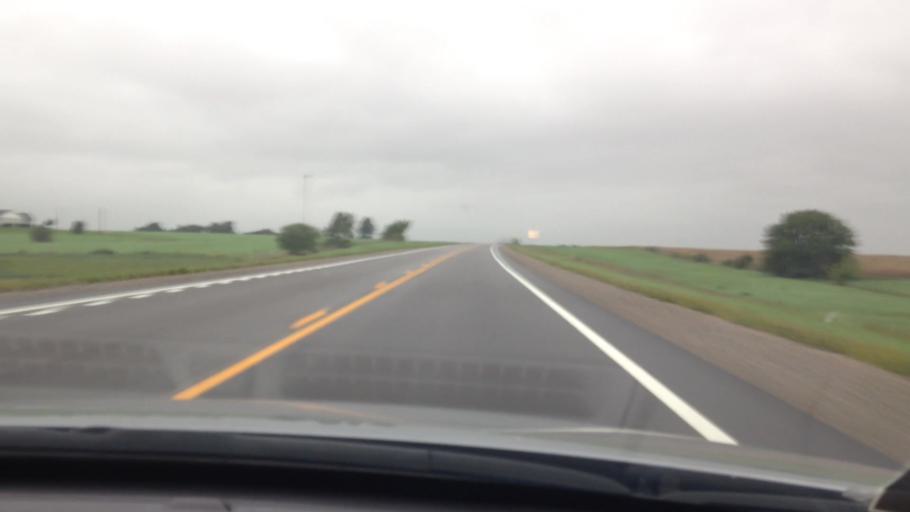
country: US
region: Kansas
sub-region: Brown County
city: Hiawatha
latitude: 39.8412
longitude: -95.5530
